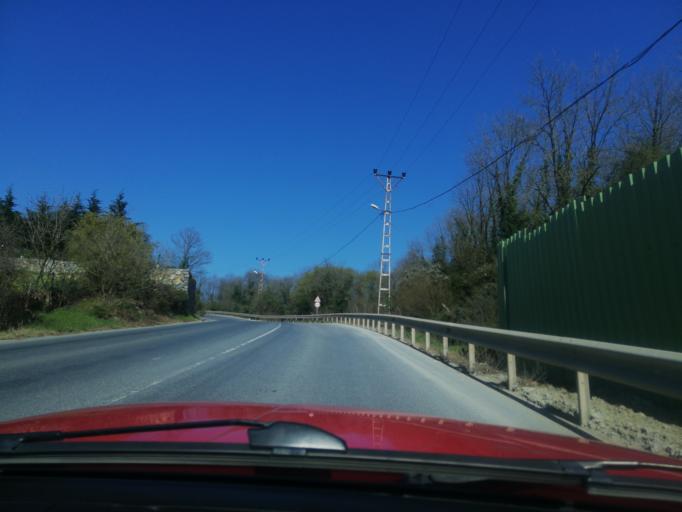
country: TR
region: Istanbul
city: Mahmut Sevket Pasa
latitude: 41.1034
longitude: 29.1590
